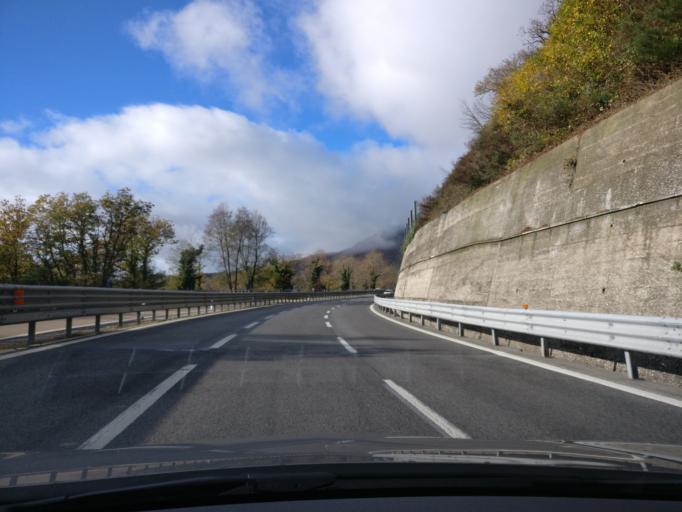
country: IT
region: Campania
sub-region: Provincia di Avellino
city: Monteforte Irpino
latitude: 40.8967
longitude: 14.7269
